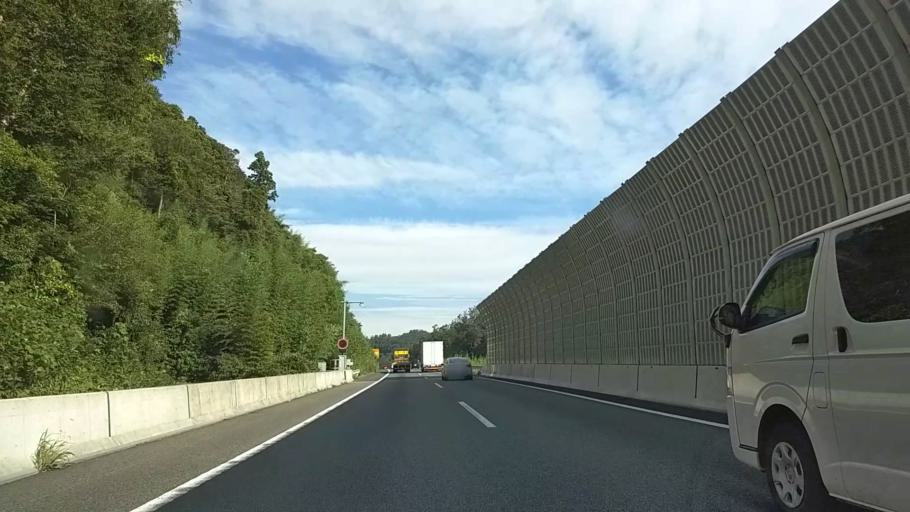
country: JP
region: Kanagawa
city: Zama
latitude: 35.5512
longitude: 139.3178
